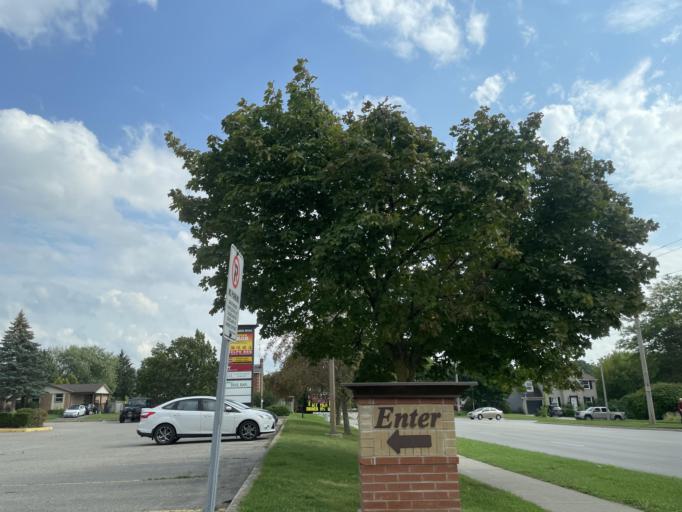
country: CA
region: Ontario
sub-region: Wellington County
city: Guelph
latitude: 43.5145
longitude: -80.2378
